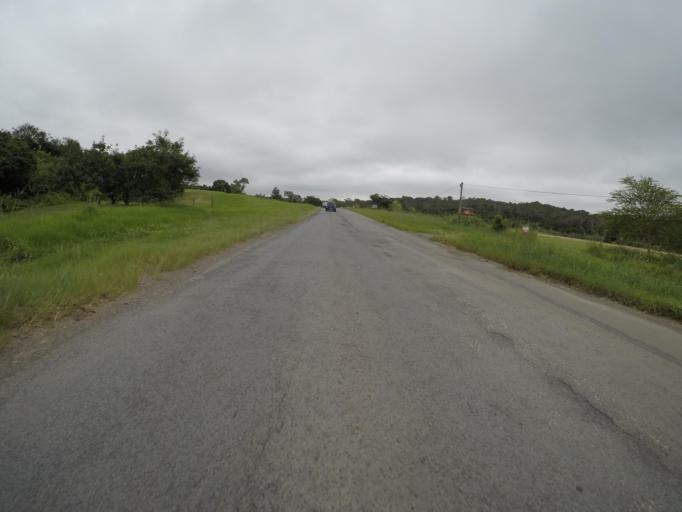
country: ZA
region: Eastern Cape
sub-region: Buffalo City Metropolitan Municipality
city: East London
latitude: -32.9409
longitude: 27.9380
